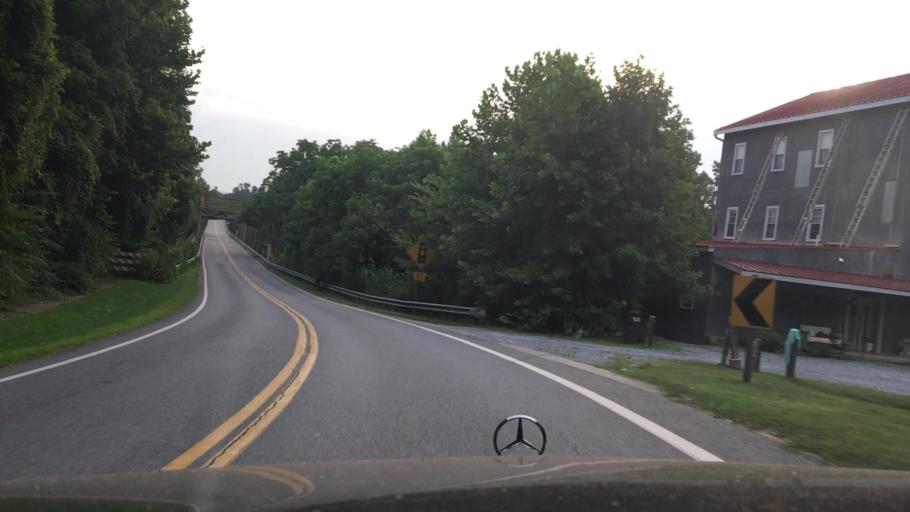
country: US
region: Virginia
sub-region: Pittsylvania County
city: Hurt
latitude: 37.1036
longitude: -79.2961
